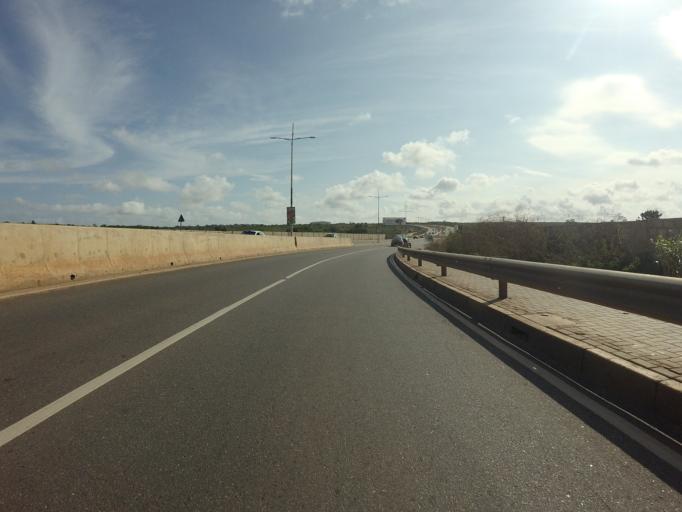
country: GH
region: Greater Accra
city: Medina Estates
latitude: 5.6173
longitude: -0.1530
